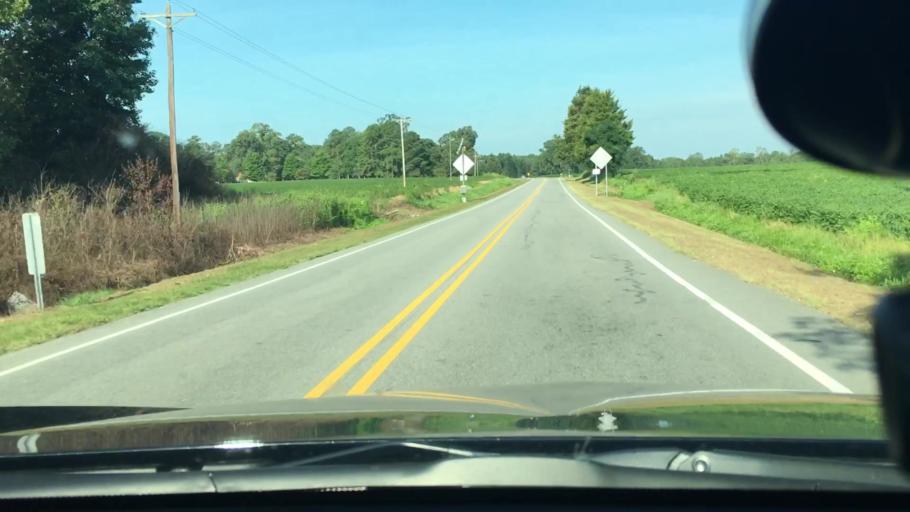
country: US
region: North Carolina
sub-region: Edgecombe County
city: Pinetops
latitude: 35.7815
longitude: -77.6068
